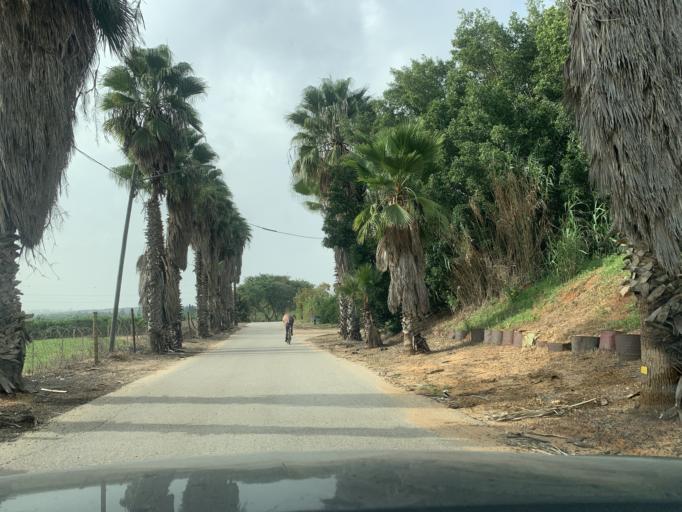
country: IL
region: Central District
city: Tirah
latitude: 32.2143
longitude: 34.9375
